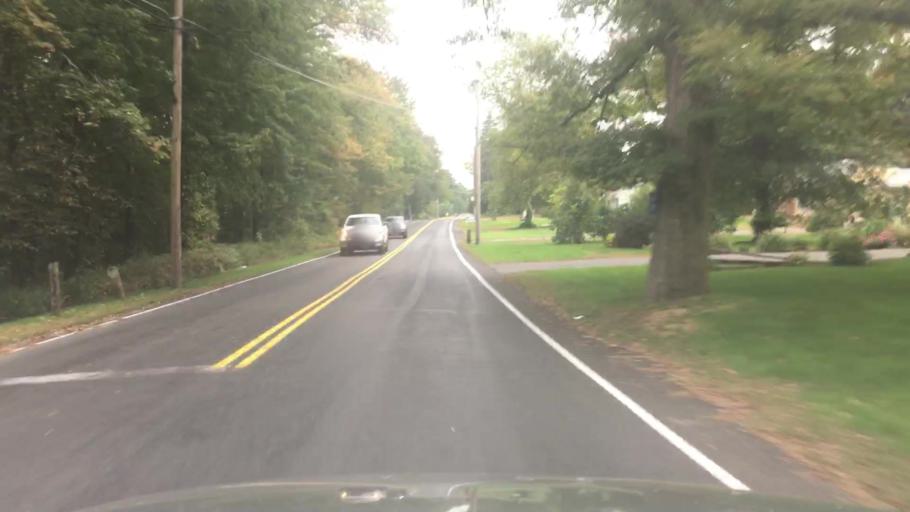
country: US
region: Connecticut
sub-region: Tolland County
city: Somers
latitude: 41.9953
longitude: -72.4561
